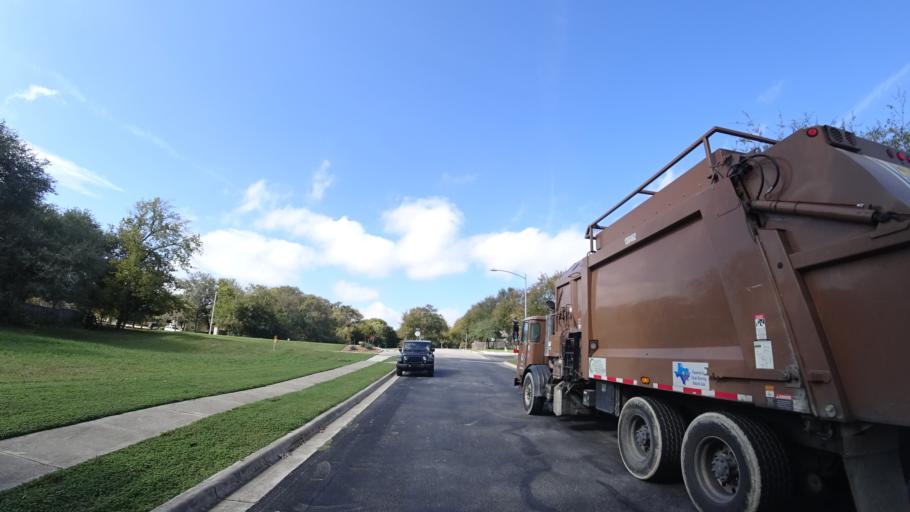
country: US
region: Texas
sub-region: Travis County
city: Shady Hollow
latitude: 30.1898
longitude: -97.8174
